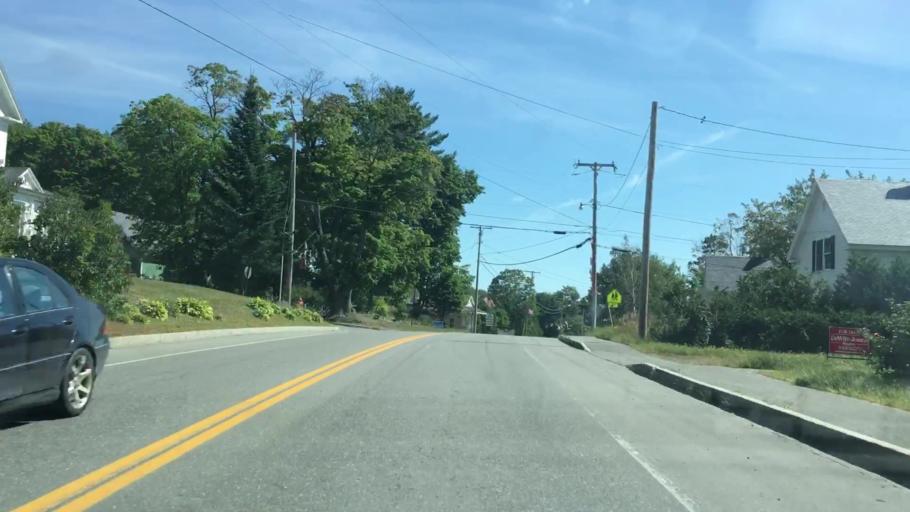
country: US
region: Maine
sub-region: Piscataquis County
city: Milo
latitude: 45.2506
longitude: -68.9825
